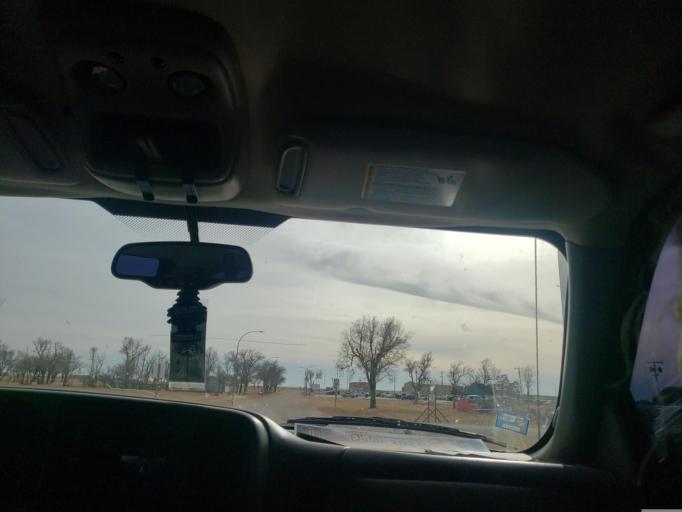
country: US
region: Kansas
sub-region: Finney County
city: Garden City
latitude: 37.9290
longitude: -100.7182
